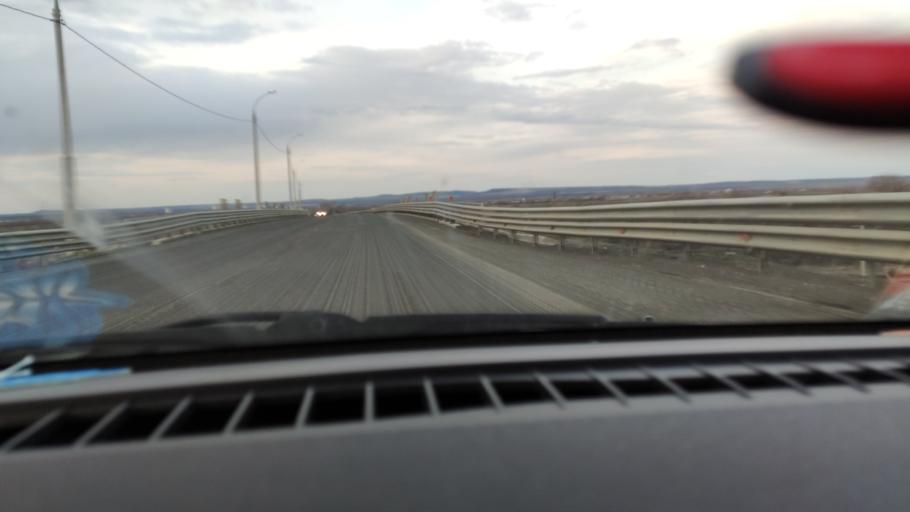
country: RU
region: Saratov
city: Yelshanka
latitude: 51.8043
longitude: 46.1925
